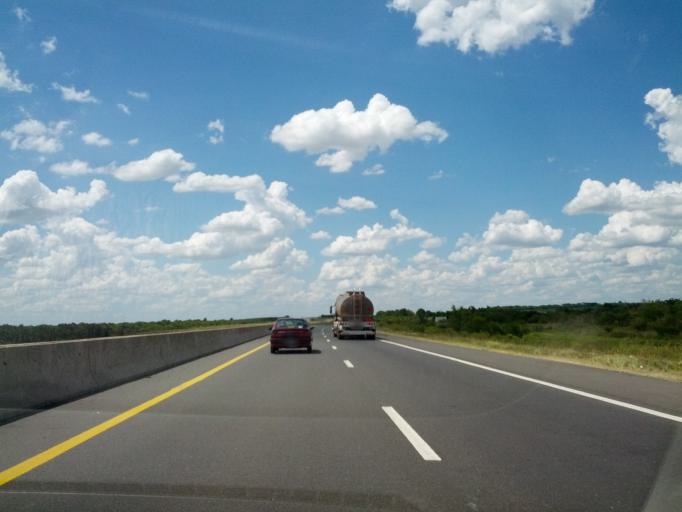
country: AR
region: Entre Rios
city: Colonia Elia
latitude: -32.7510
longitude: -58.4839
